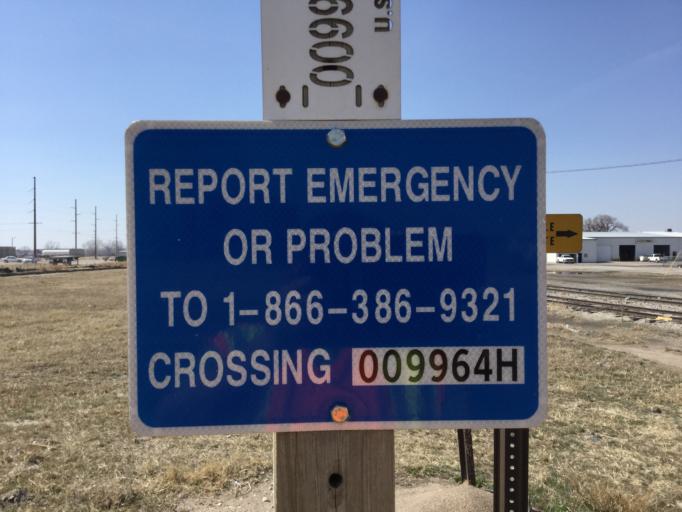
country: US
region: Kansas
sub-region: Barton County
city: Great Bend
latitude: 38.3560
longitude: -98.7652
